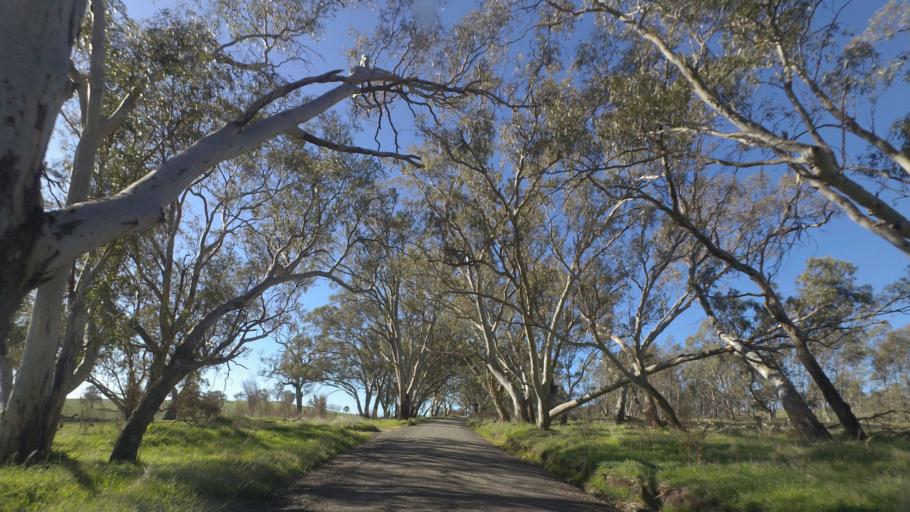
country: AU
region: Victoria
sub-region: Mount Alexander
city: Castlemaine
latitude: -36.9624
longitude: 144.3308
